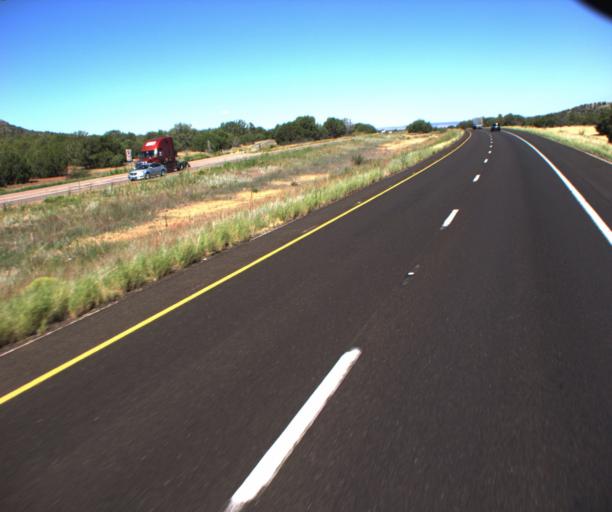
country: US
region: Arizona
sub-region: Yavapai County
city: Paulden
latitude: 35.2683
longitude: -112.7272
